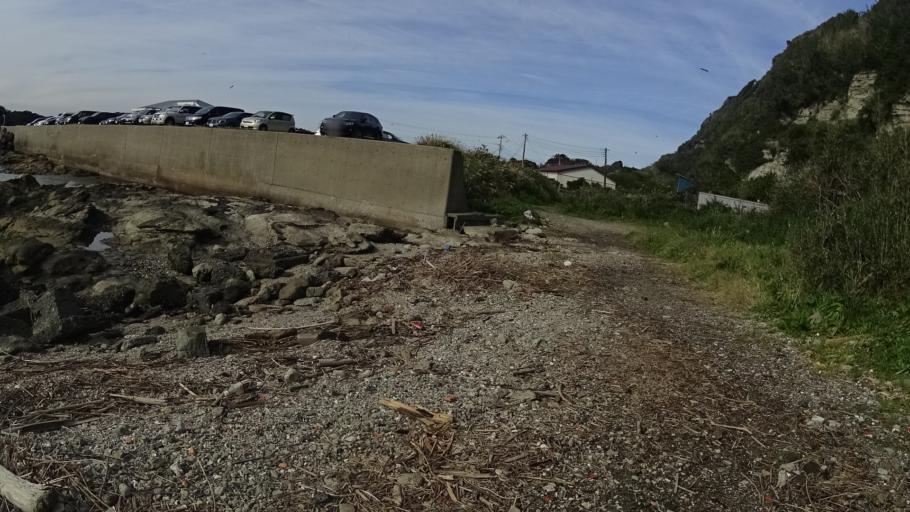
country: JP
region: Kanagawa
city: Miura
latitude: 35.1426
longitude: 139.6692
